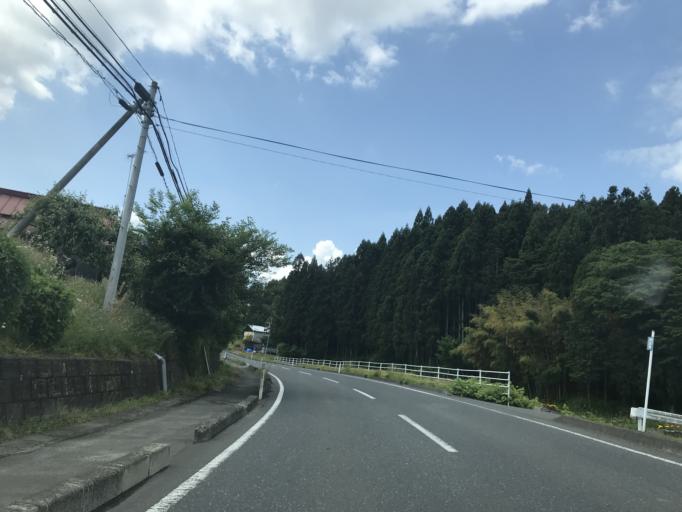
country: JP
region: Miyagi
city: Furukawa
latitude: 38.7526
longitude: 140.9544
